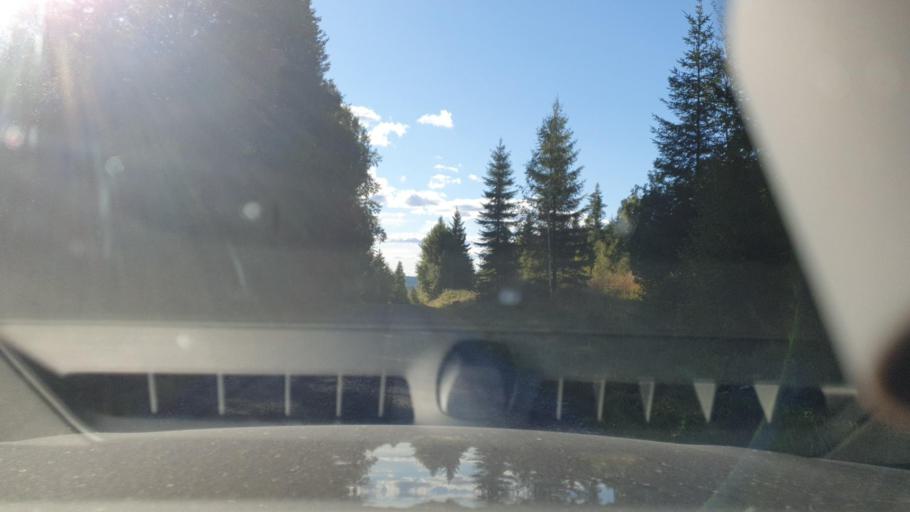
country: SE
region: Vaermland
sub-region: Filipstads Kommun
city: Filipstad
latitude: 59.8143
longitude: 13.9542
